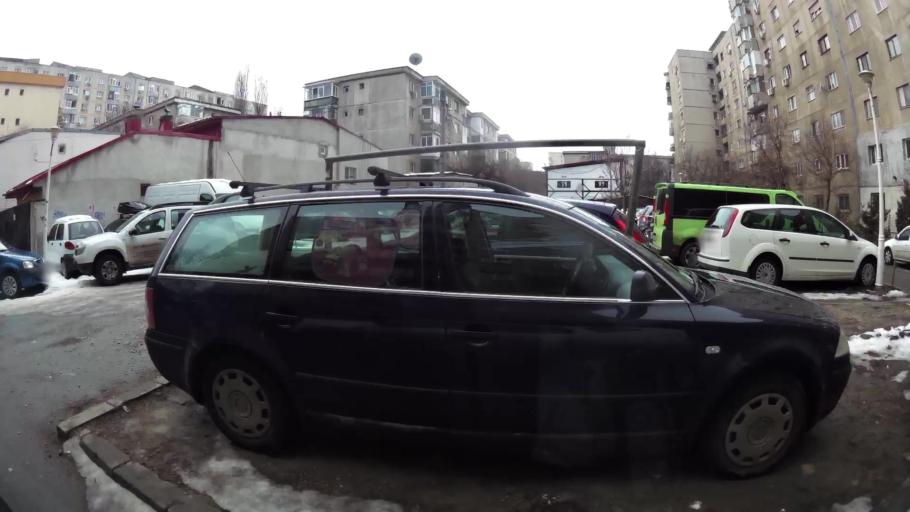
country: RO
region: Bucuresti
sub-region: Municipiul Bucuresti
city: Bucuresti
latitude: 44.4125
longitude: 26.0699
